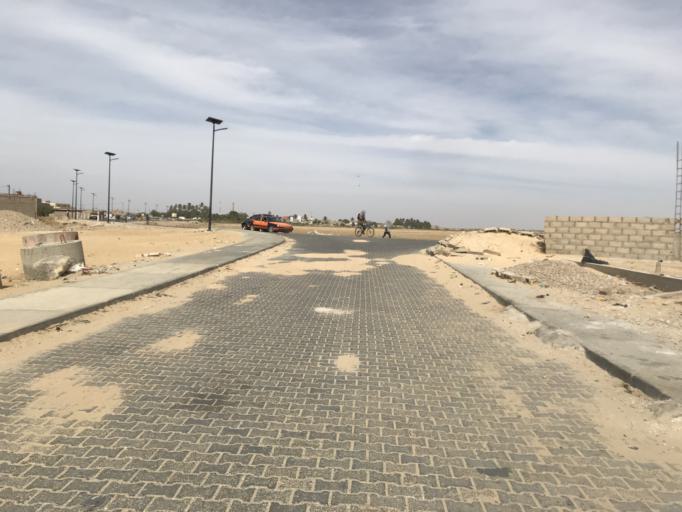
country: SN
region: Saint-Louis
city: Saint-Louis
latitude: 16.0234
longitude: -16.4830
